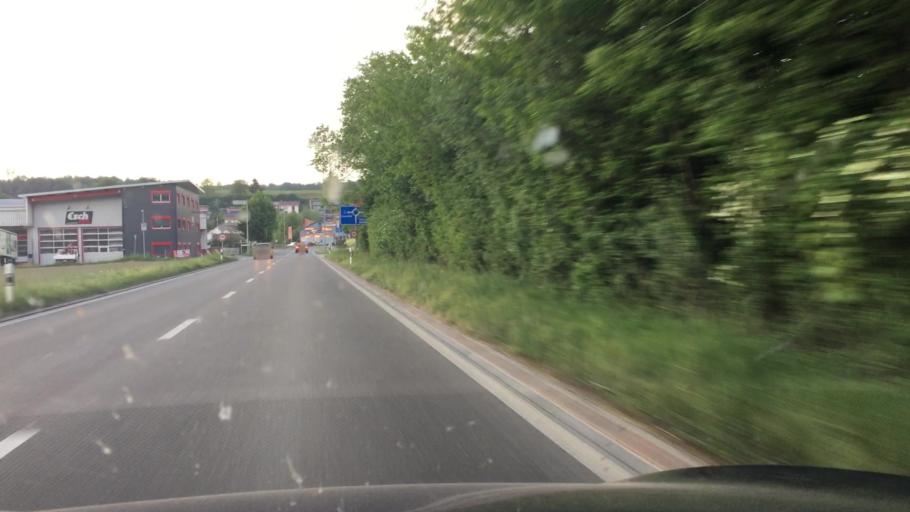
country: CH
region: Thurgau
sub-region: Frauenfeld District
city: Mullheim
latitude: 47.5976
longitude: 8.9961
